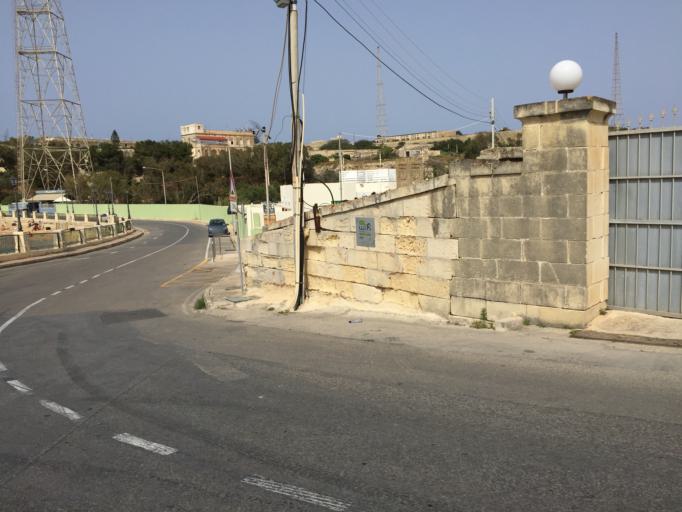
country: MT
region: Il-Kalkara
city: Kalkara
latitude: 35.8928
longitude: 14.5270
